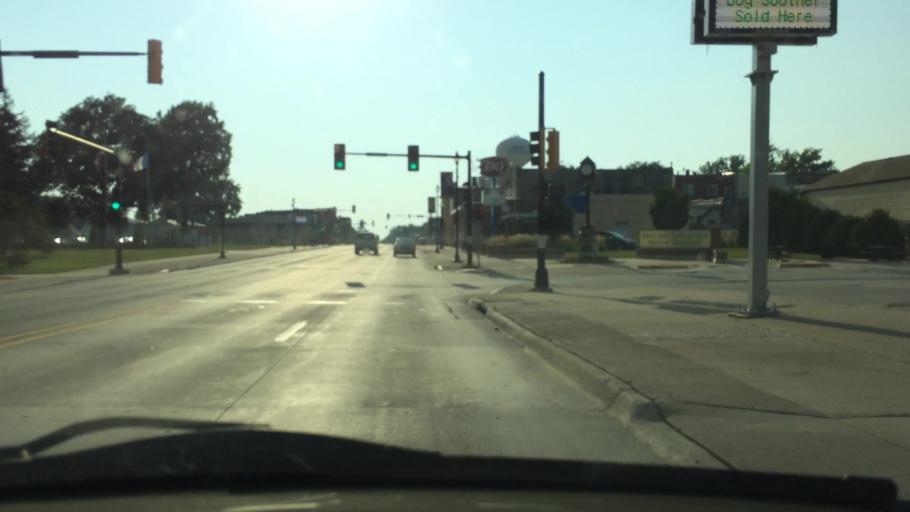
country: US
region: Iowa
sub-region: Henry County
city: Mount Pleasant
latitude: 40.9653
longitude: -91.5516
